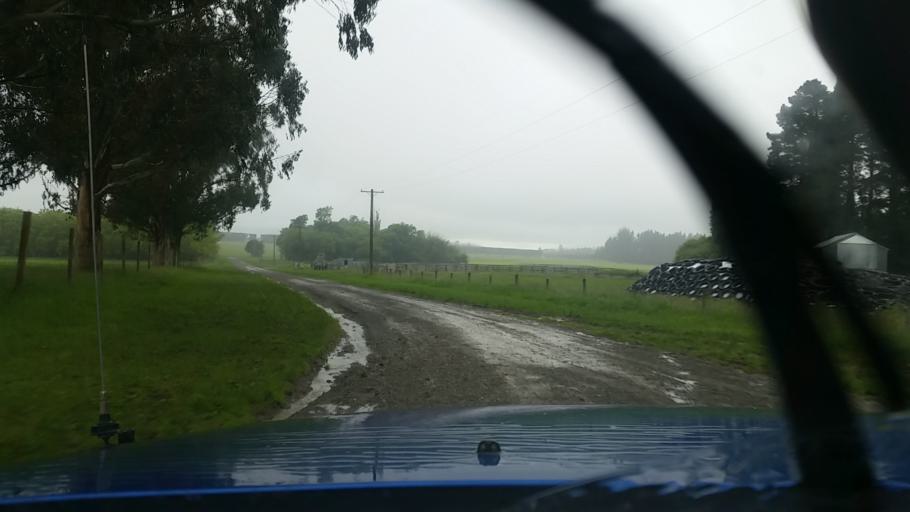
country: NZ
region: Canterbury
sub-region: Ashburton District
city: Methven
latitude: -43.7537
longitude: 171.2540
